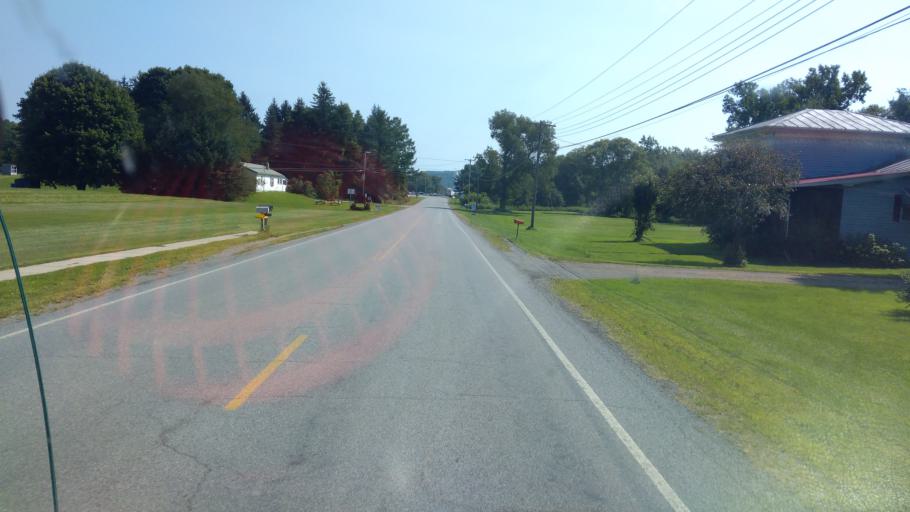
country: US
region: New York
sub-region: Allegany County
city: Friendship
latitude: 42.2131
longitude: -78.1218
